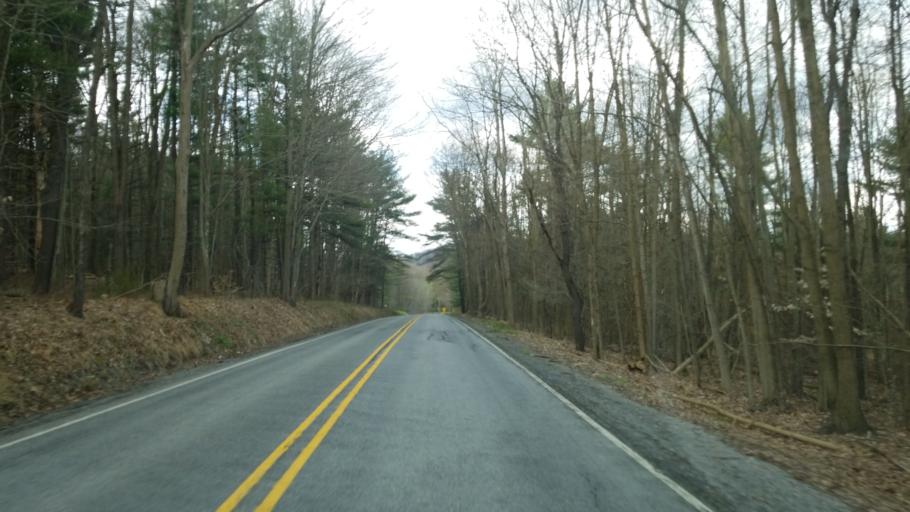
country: US
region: Pennsylvania
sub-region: Clearfield County
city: Curwensville
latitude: 40.8921
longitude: -78.4636
